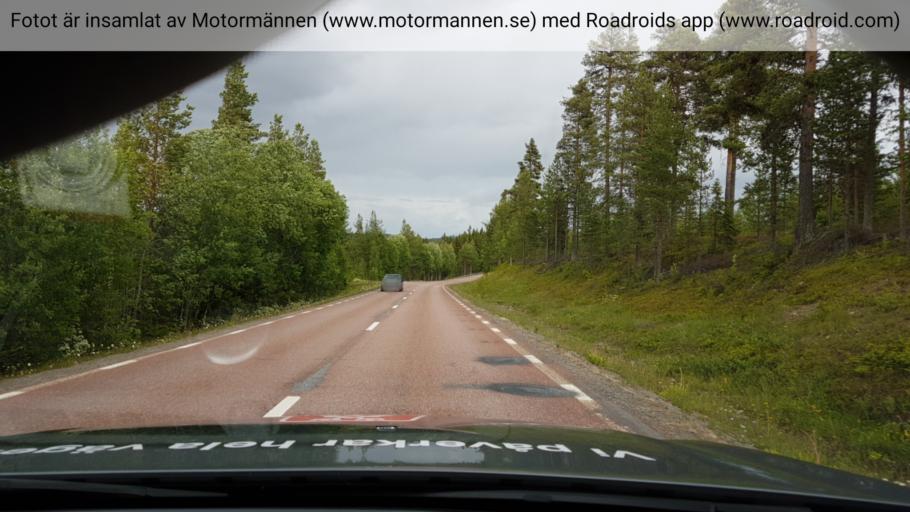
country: SE
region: Vaesterbotten
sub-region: Dorotea Kommun
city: Dorotea
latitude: 64.1071
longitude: 16.1299
